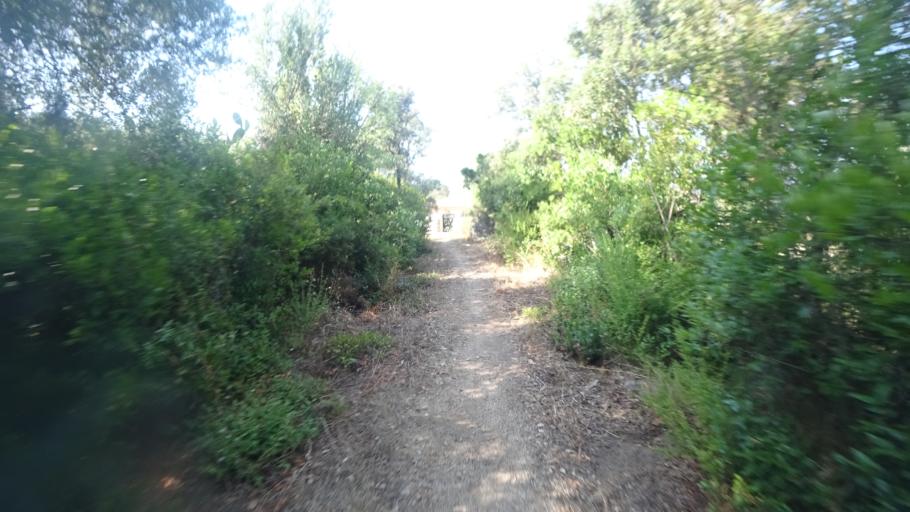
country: FR
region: Corsica
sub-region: Departement de la Corse-du-Sud
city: Porto-Vecchio
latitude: 41.6633
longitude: 9.3273
